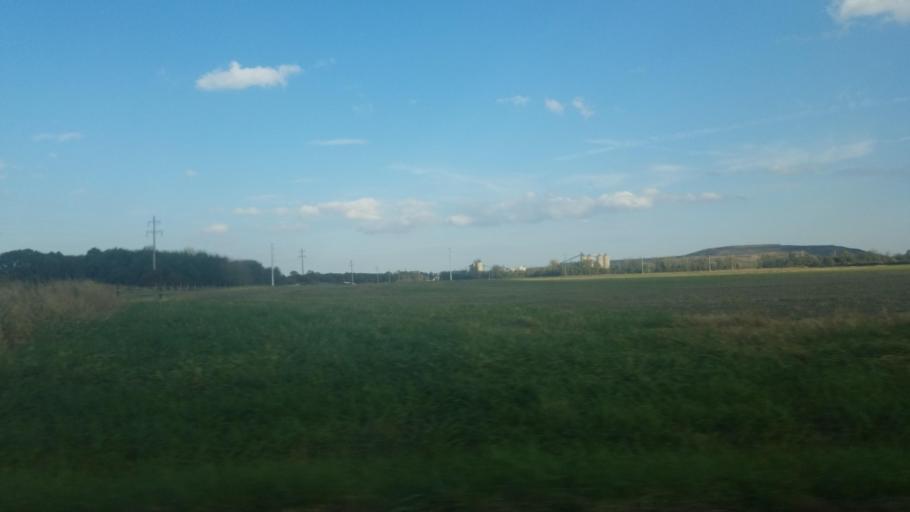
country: US
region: Illinois
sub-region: Saline County
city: Harrisburg
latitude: 37.8265
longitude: -88.6146
